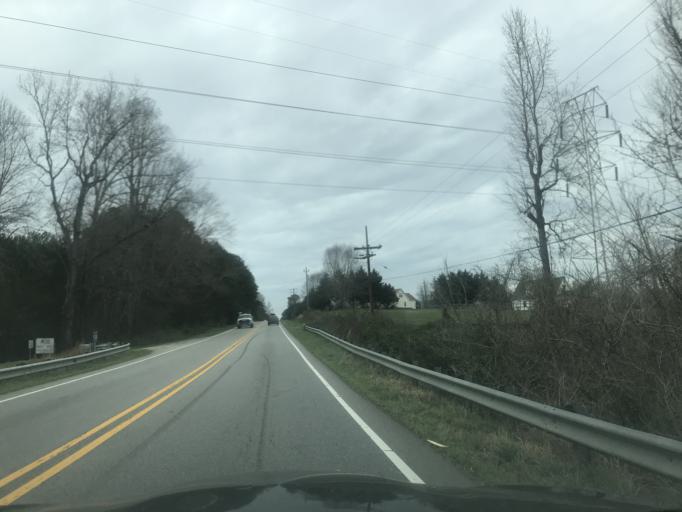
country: US
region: North Carolina
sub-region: Franklin County
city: Franklinton
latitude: 36.1071
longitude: -78.4714
